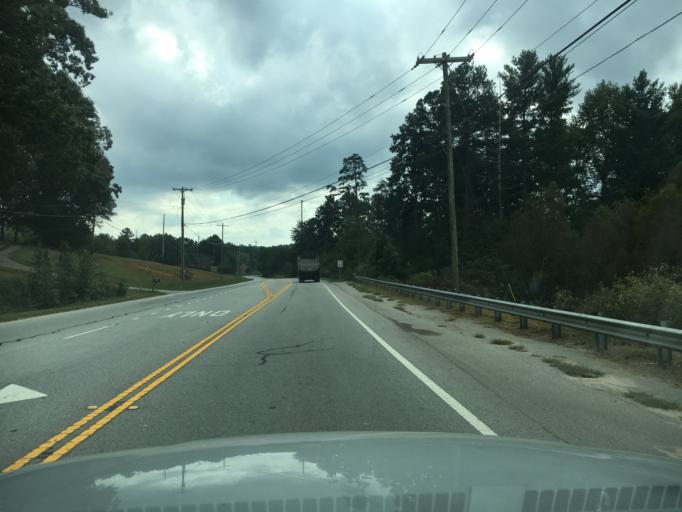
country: US
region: South Carolina
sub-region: Greenville County
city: Greer
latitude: 34.9640
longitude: -82.2343
